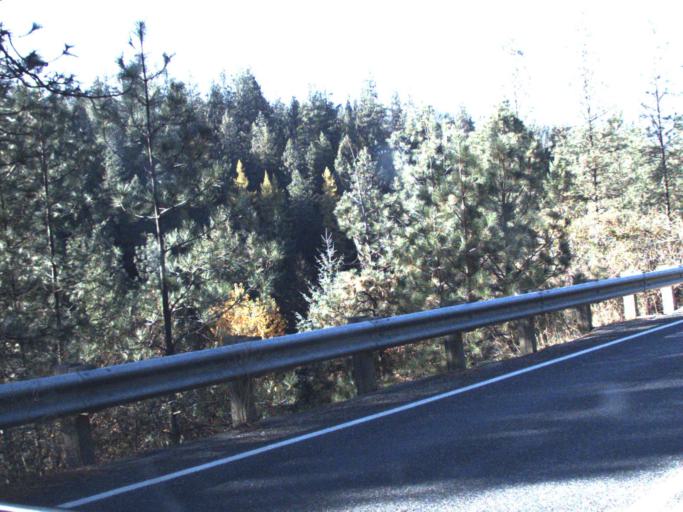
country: US
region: Washington
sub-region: Stevens County
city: Kettle Falls
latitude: 48.6082
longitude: -118.0756
